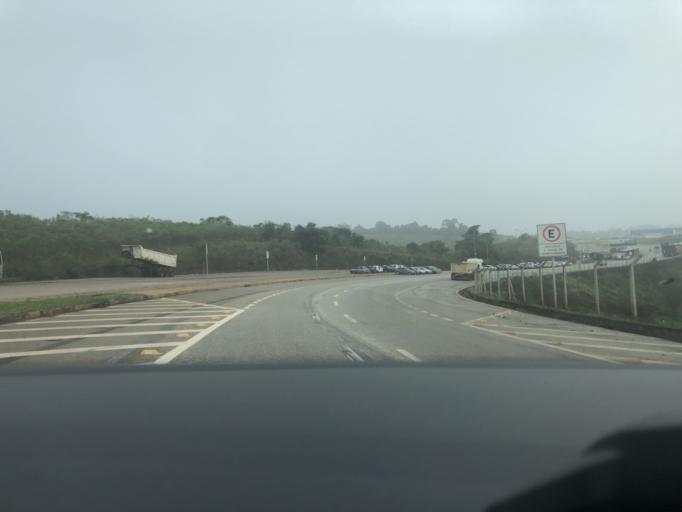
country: BR
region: Minas Gerais
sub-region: Congonhas
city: Congonhas
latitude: -20.5956
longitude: -43.9575
